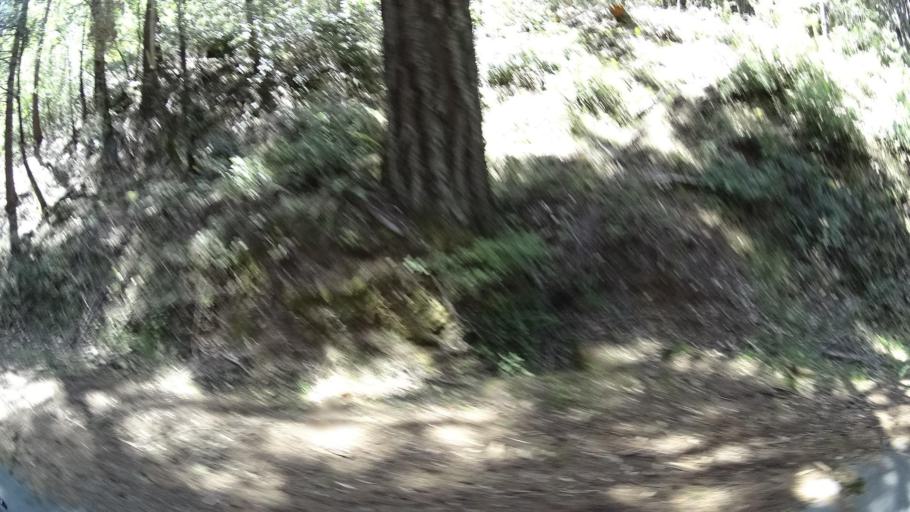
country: US
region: California
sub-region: Humboldt County
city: Rio Dell
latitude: 40.3091
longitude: -124.0626
